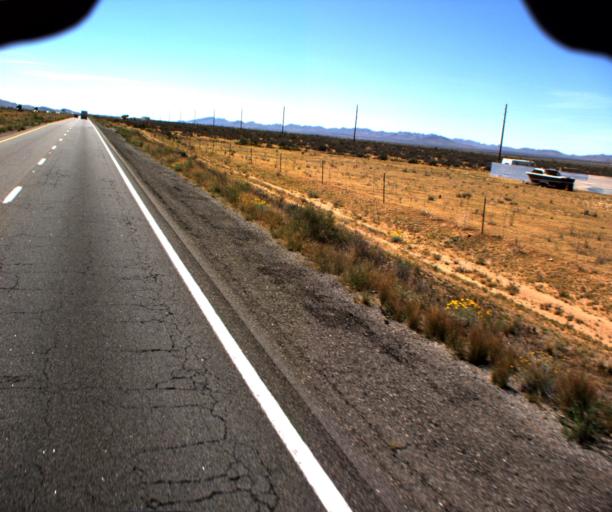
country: US
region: Arizona
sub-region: Mohave County
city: Dolan Springs
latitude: 35.5527
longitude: -114.3686
